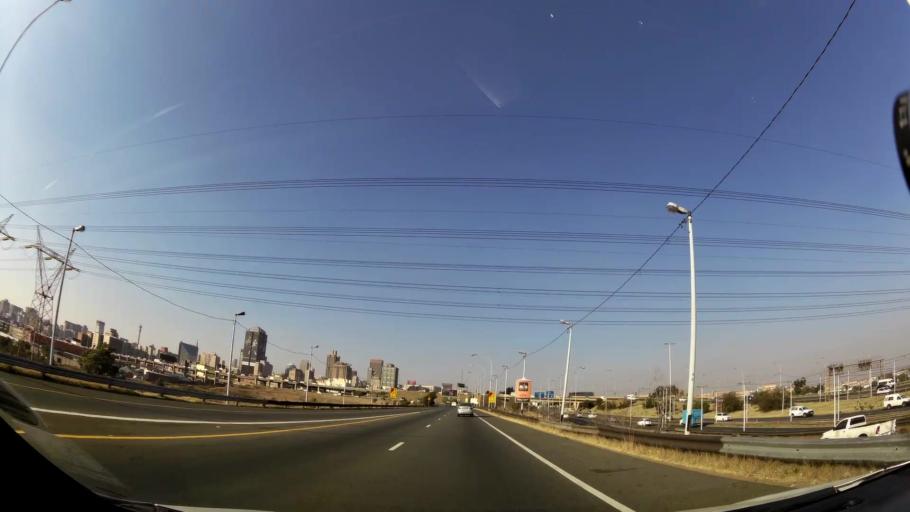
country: ZA
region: Gauteng
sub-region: City of Johannesburg Metropolitan Municipality
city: Johannesburg
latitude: -26.2112
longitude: 28.0275
